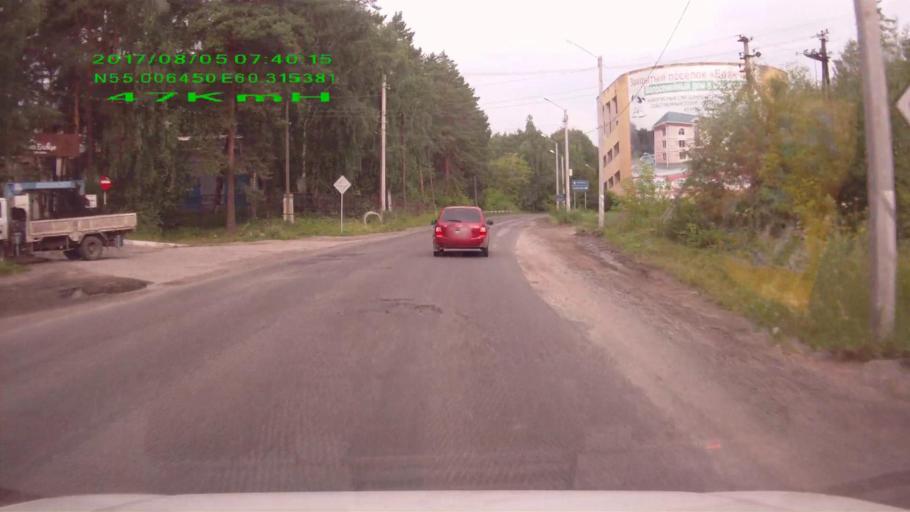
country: RU
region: Chelyabinsk
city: Chebarkul'
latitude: 55.0065
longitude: 60.3151
